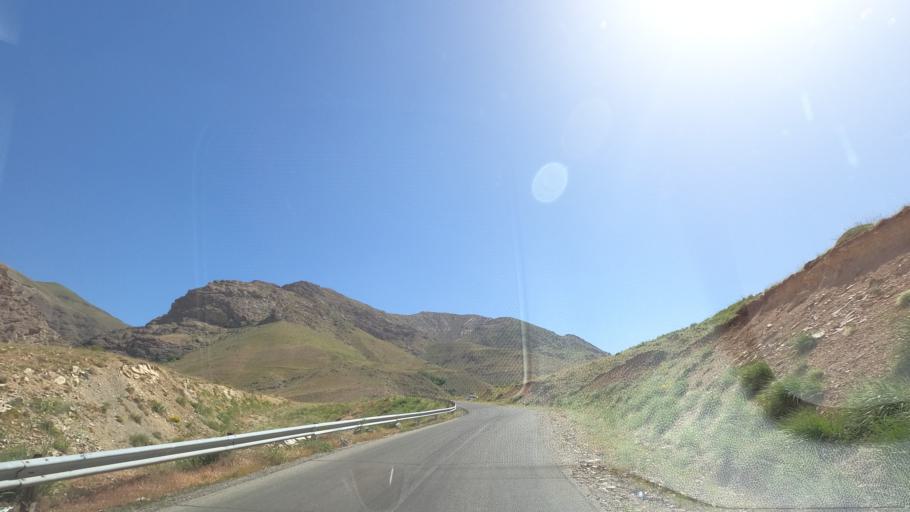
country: IR
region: Alborz
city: Karaj
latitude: 35.9241
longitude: 51.1561
